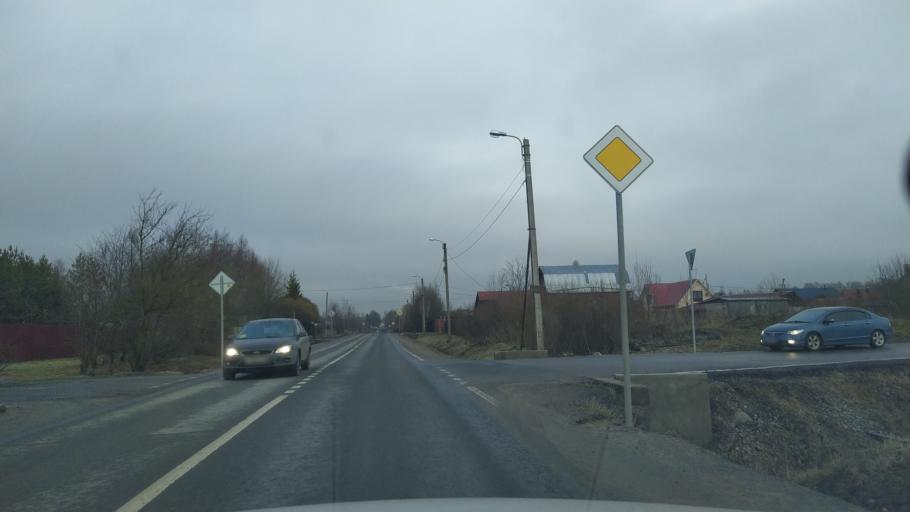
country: RU
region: St.-Petersburg
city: Aleksandrovskaya
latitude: 59.7220
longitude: 30.3459
